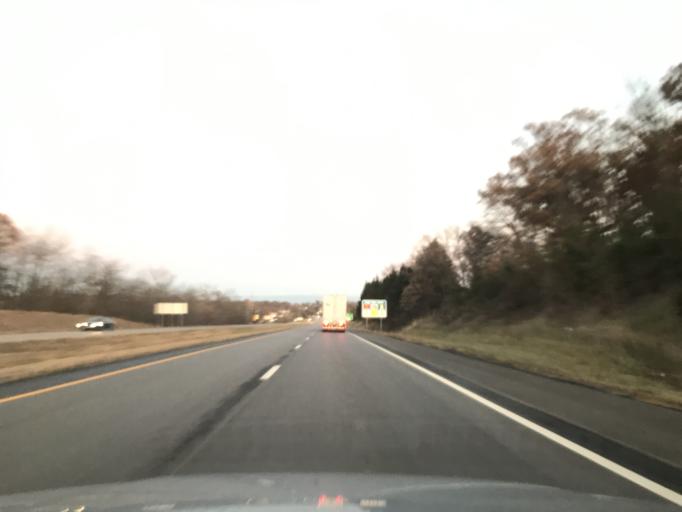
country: US
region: Missouri
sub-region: Marion County
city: Hannibal
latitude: 39.7144
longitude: -91.4057
